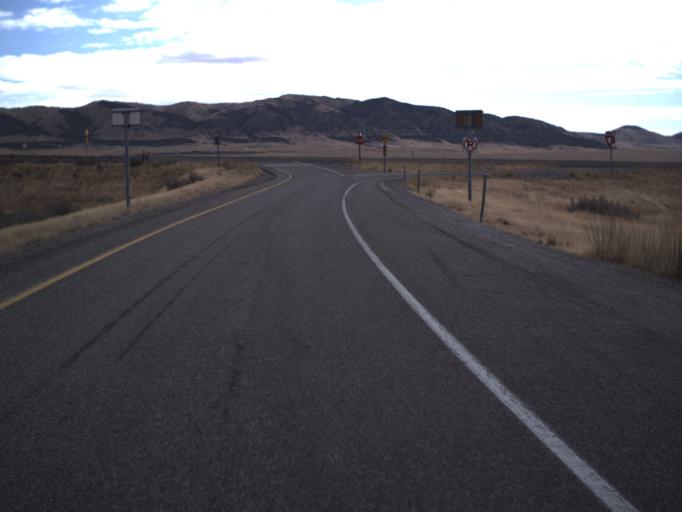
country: US
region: Idaho
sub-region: Oneida County
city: Malad City
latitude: 41.9648
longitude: -112.7605
